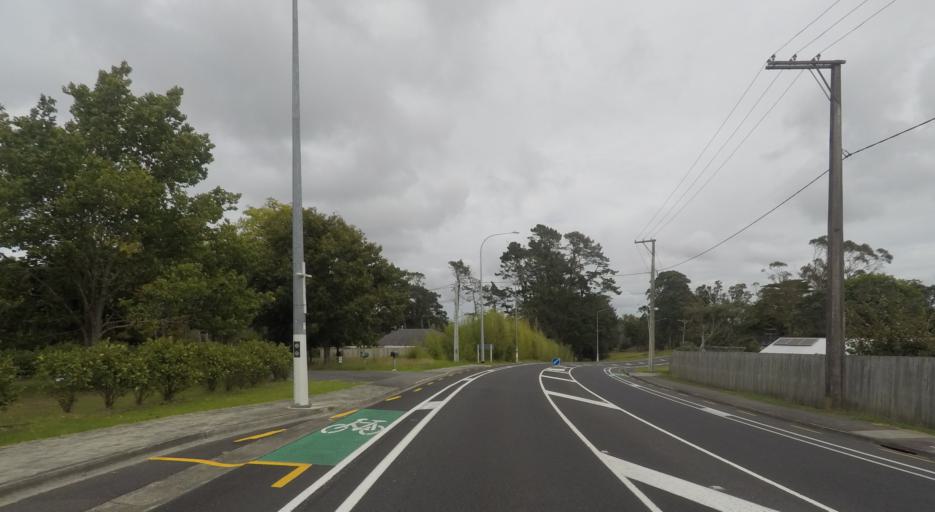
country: NZ
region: Auckland
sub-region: Auckland
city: North Shore
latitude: -36.7771
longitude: 174.6907
